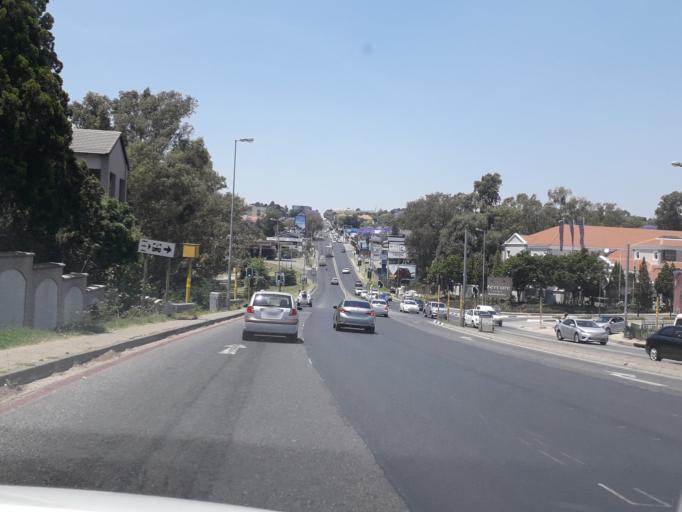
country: ZA
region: Gauteng
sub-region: City of Johannesburg Metropolitan Municipality
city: Johannesburg
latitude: -26.0982
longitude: 27.9897
